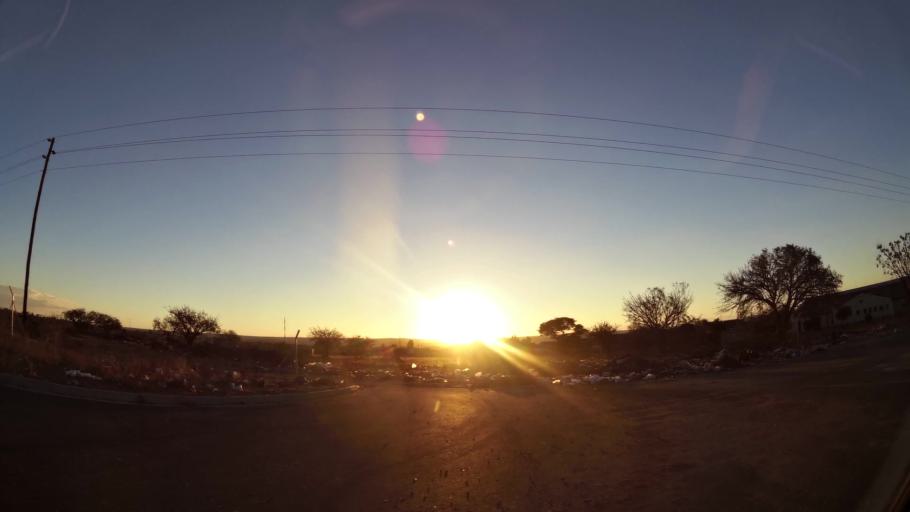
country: ZA
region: Limpopo
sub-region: Capricorn District Municipality
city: Polokwane
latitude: -23.8582
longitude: 29.3753
